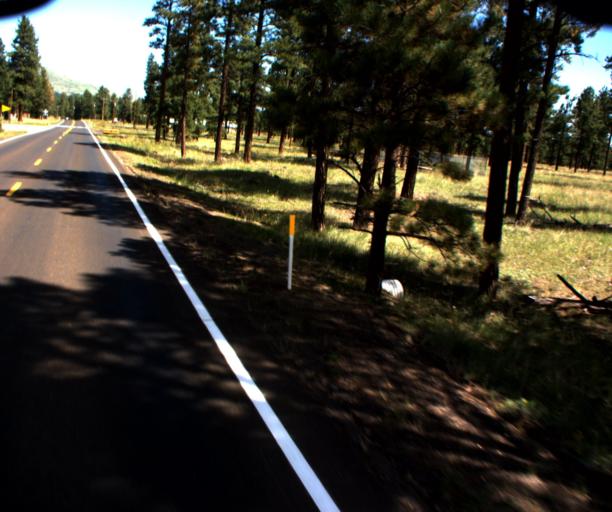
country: US
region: Arizona
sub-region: Apache County
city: Eagar
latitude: 34.0519
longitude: -109.4604
